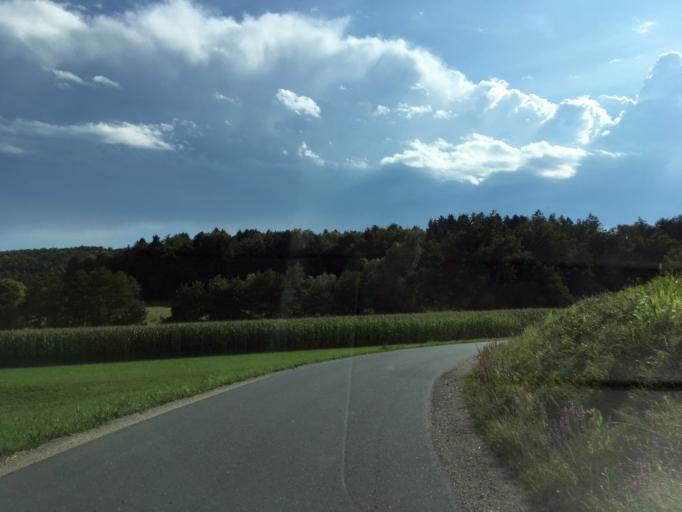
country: AT
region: Styria
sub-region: Politischer Bezirk Leibnitz
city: Sankt Nikolai im Sausal
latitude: 46.8142
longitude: 15.4556
